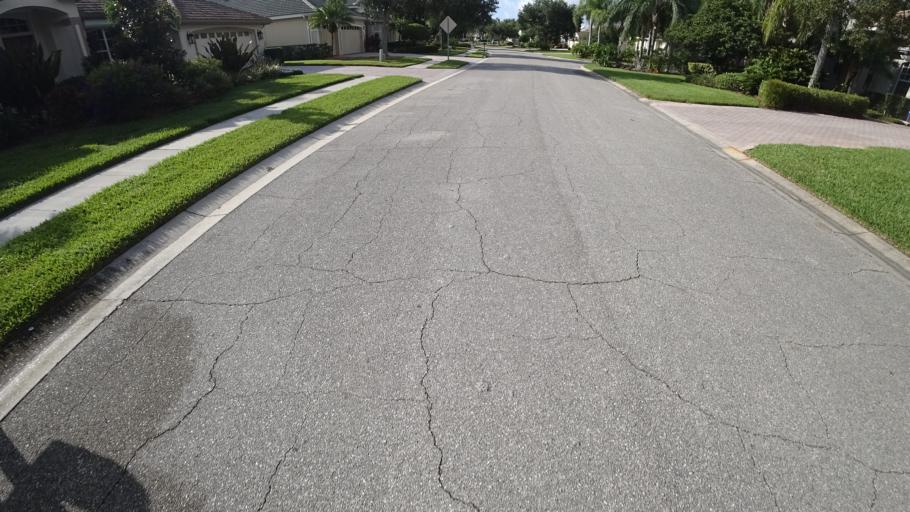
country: US
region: Florida
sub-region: Sarasota County
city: Desoto Lakes
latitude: 27.4188
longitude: -82.4750
